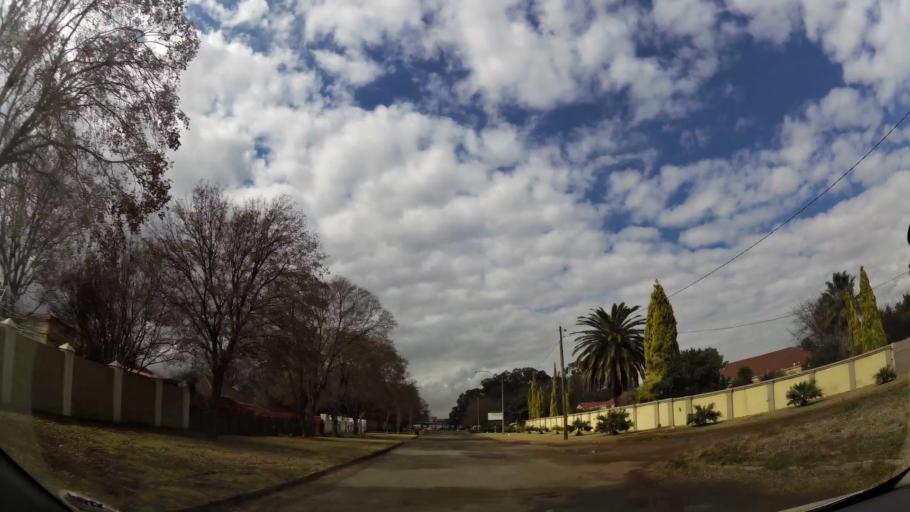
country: ZA
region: Gauteng
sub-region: Sedibeng District Municipality
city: Vereeniging
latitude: -26.6554
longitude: 27.9933
